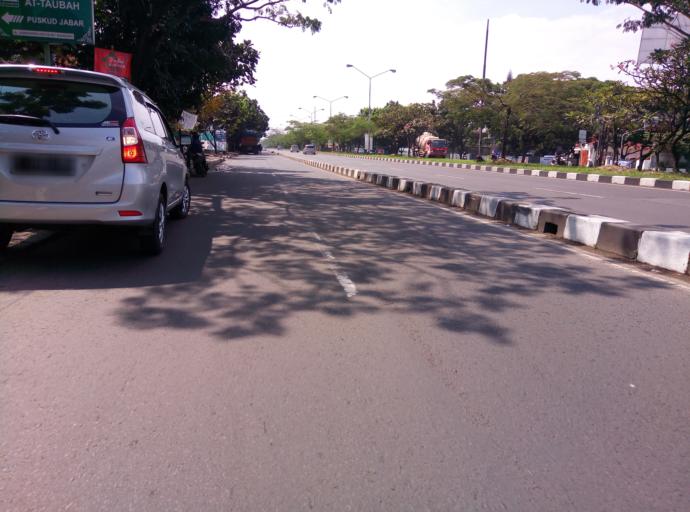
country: ID
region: West Java
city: Bandung
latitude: -6.9427
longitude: 107.6500
